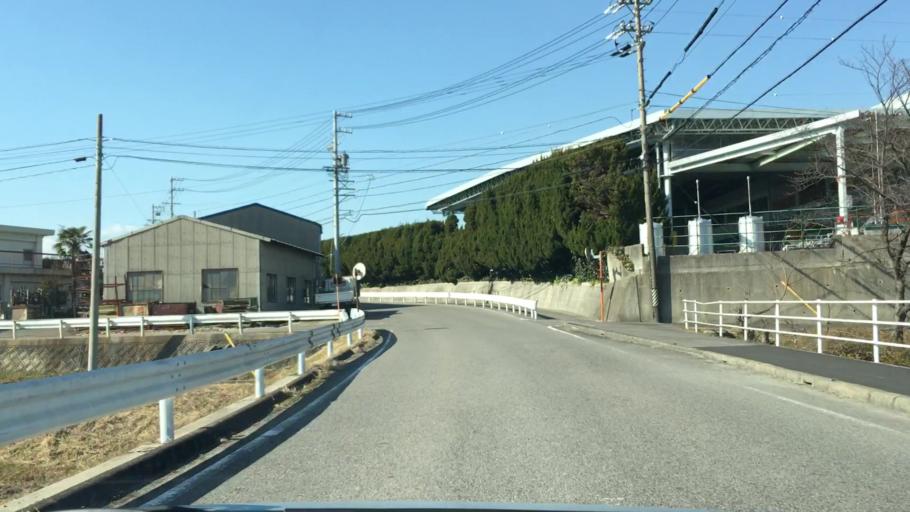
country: JP
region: Aichi
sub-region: Toyota-shi
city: Toyota
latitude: 35.0334
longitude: 137.1272
